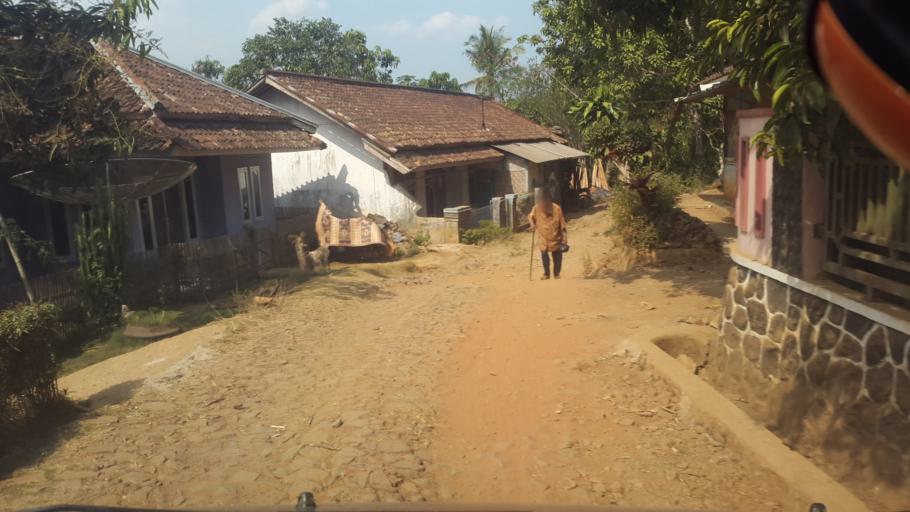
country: ID
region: West Java
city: Nangerang
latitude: -7.1121
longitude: 106.8044
